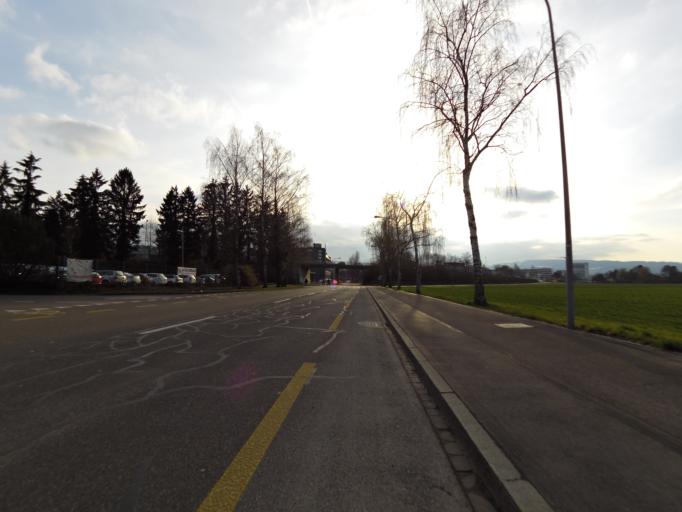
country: CH
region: Zurich
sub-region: Bezirk Dietikon
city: Schlieren / Boden
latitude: 47.4029
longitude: 8.4572
